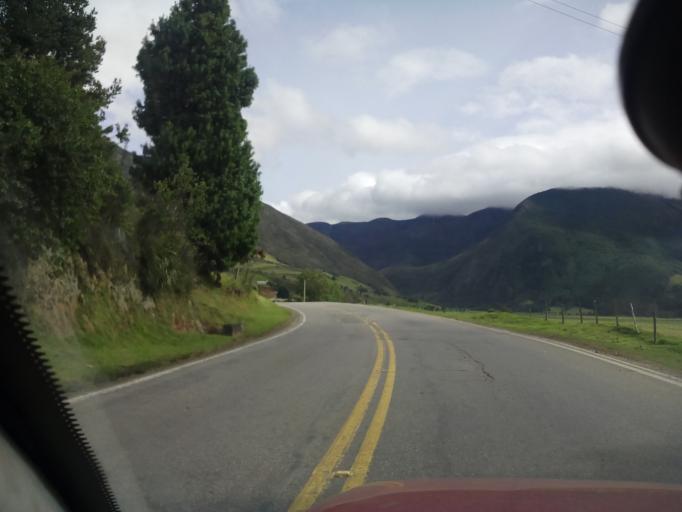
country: CO
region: Boyaca
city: Combita
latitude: 5.7008
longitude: -73.3691
